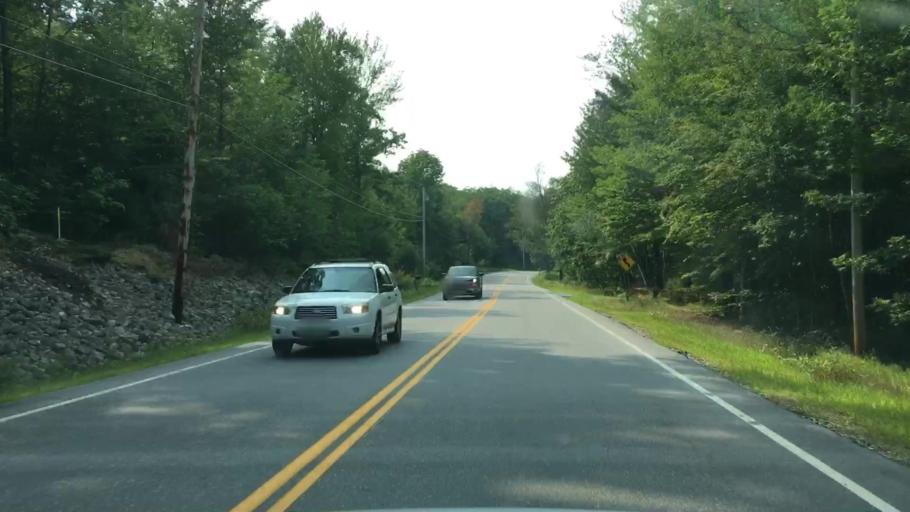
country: US
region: Maine
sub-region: Oxford County
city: Buckfield
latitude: 44.2707
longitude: -70.3964
